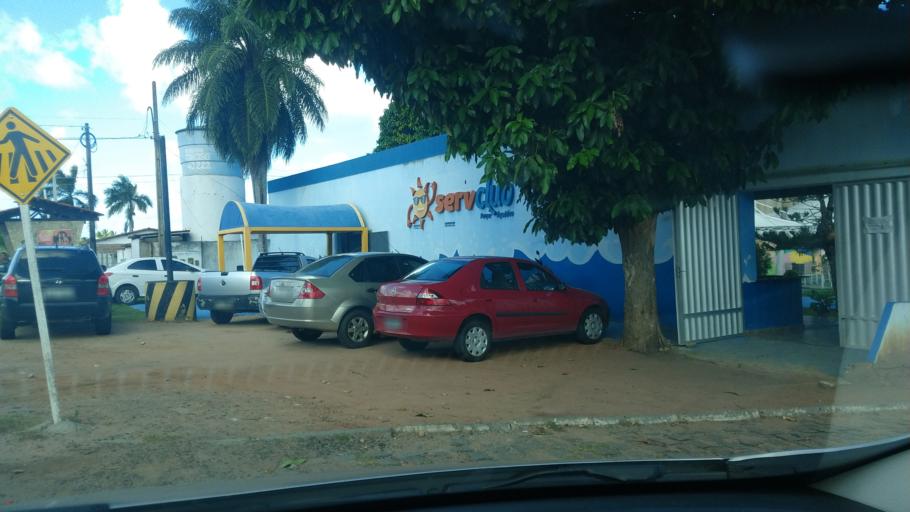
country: BR
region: Rio Grande do Norte
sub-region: Sao Goncalo Do Amarante
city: Sao Goncalo do Amarante
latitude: -5.7874
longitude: -35.2934
